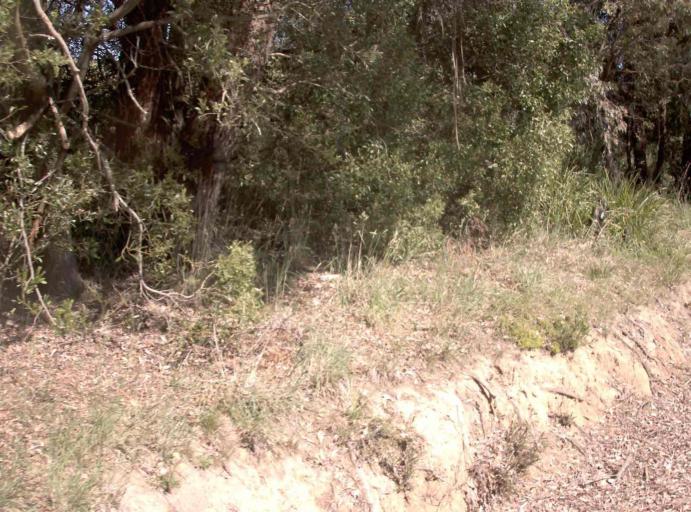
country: AU
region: New South Wales
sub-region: Bombala
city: Bombala
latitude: -37.1770
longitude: 148.7250
